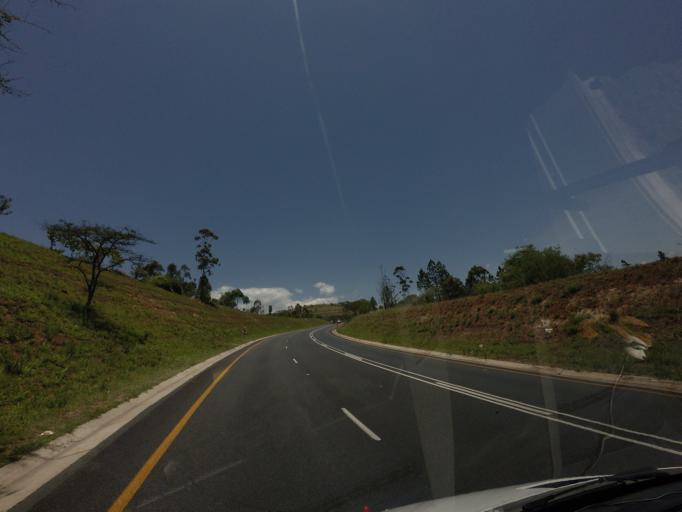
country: ZA
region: Mpumalanga
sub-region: Ehlanzeni District
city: Nelspruit
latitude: -25.4562
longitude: 30.6845
